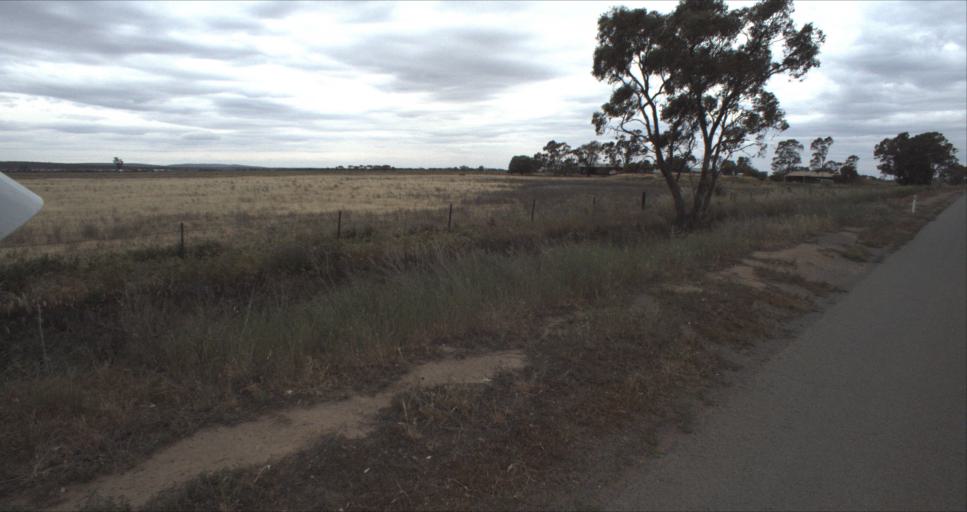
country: AU
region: New South Wales
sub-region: Leeton
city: Leeton
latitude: -34.4188
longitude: 146.3389
